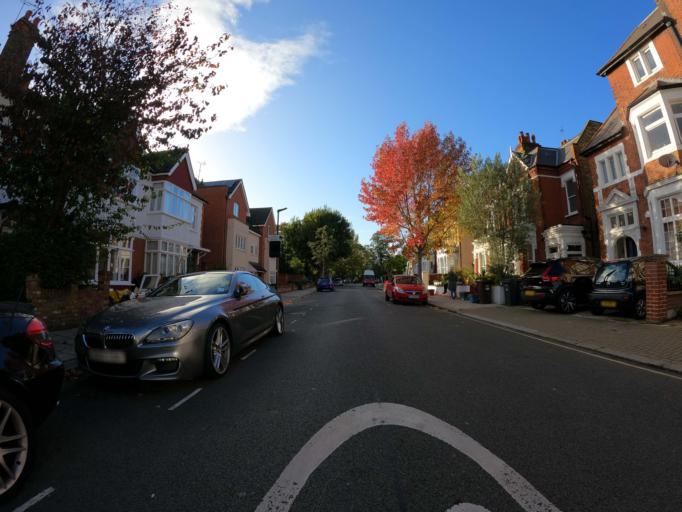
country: GB
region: England
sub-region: Greater London
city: Acton
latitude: 51.4893
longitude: -0.2840
